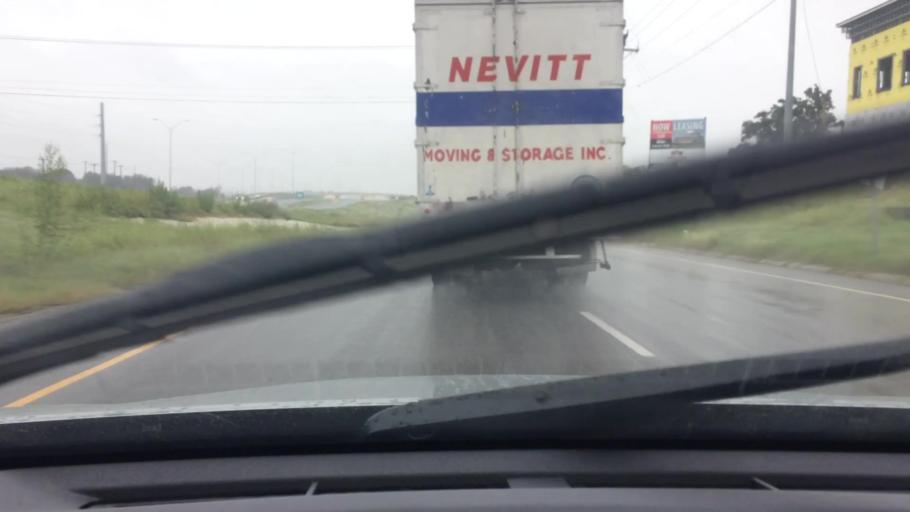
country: US
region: Texas
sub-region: Bexar County
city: Leon Valley
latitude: 29.4805
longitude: -98.7034
